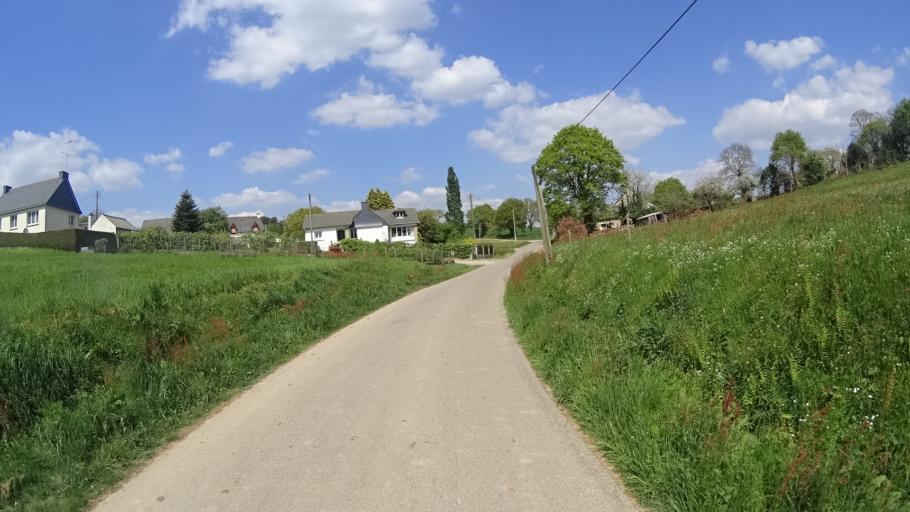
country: FR
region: Brittany
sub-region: Departement du Morbihan
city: Beganne
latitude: 47.6010
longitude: -2.2096
